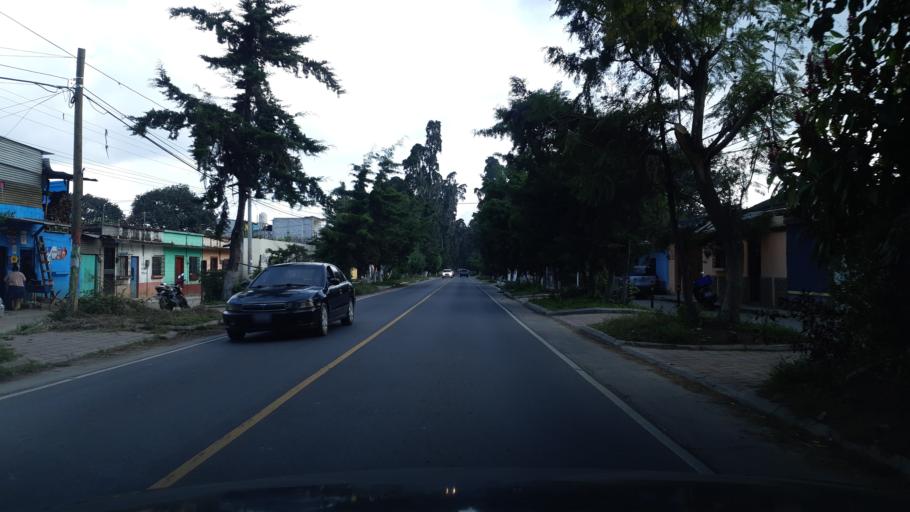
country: GT
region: Chimaltenango
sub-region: Municipio de Chimaltenango
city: Chimaltenango
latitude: 14.6506
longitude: -90.8145
